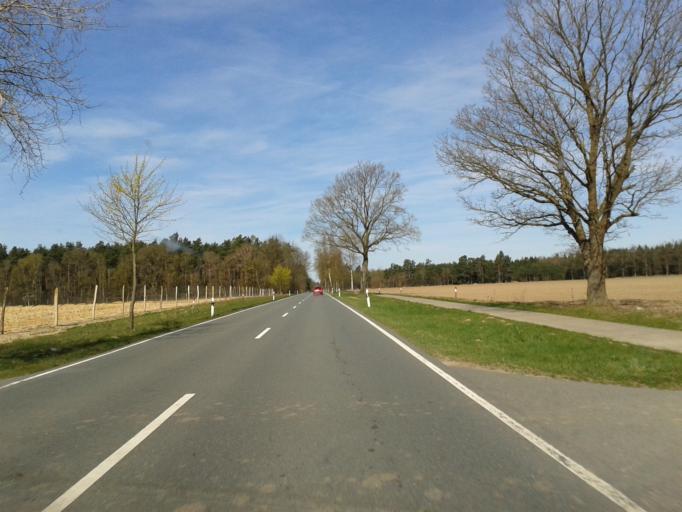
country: DE
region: Lower Saxony
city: Eimke
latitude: 52.9727
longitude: 10.2722
